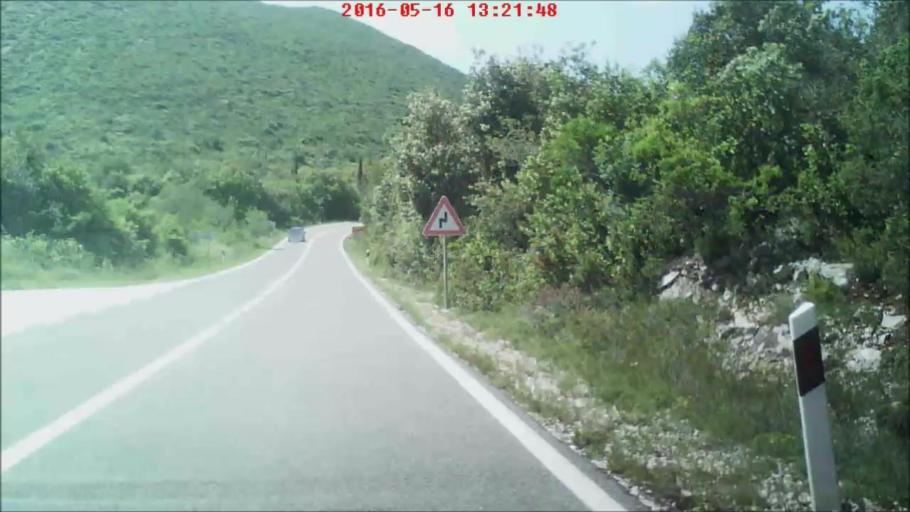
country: HR
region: Dubrovacko-Neretvanska
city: Ston
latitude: 42.8318
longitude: 17.7293
